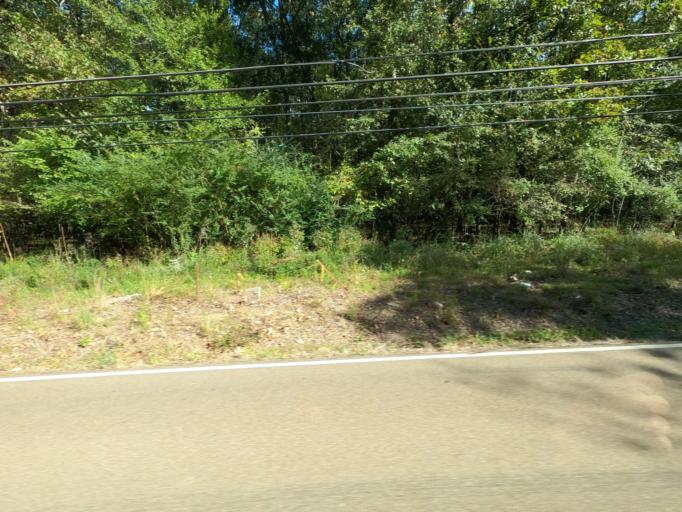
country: US
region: Tennessee
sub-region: Fayette County
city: Hickory Withe
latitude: 35.2170
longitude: -89.6504
